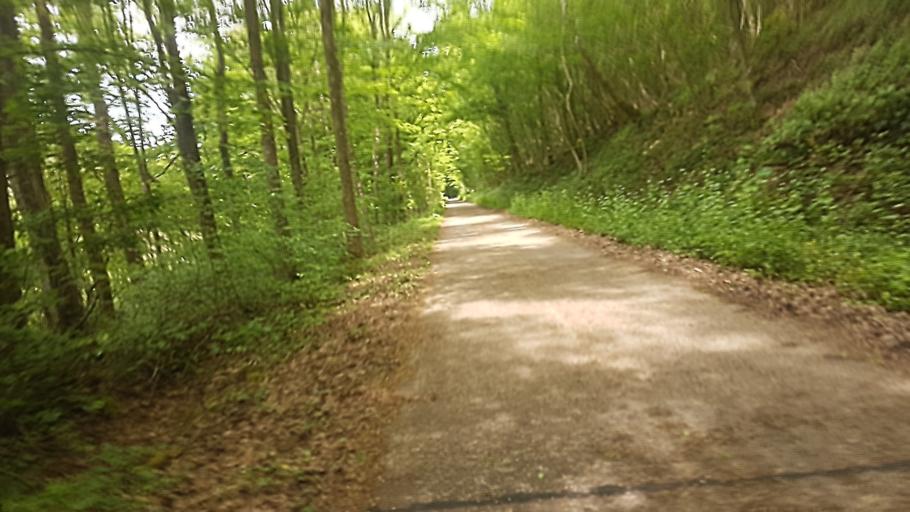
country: BE
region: Wallonia
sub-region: Province de Namur
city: Couvin
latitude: 50.0413
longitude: 4.5934
